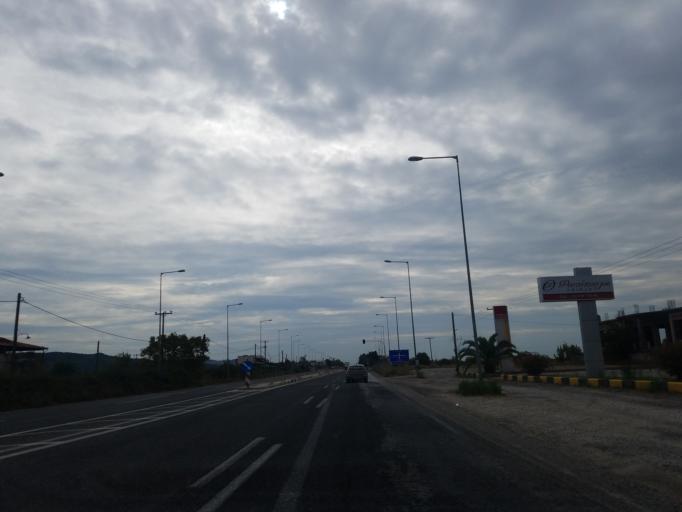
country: GR
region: Thessaly
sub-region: Trikala
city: Kalampaka
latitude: 39.6744
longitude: 21.6614
